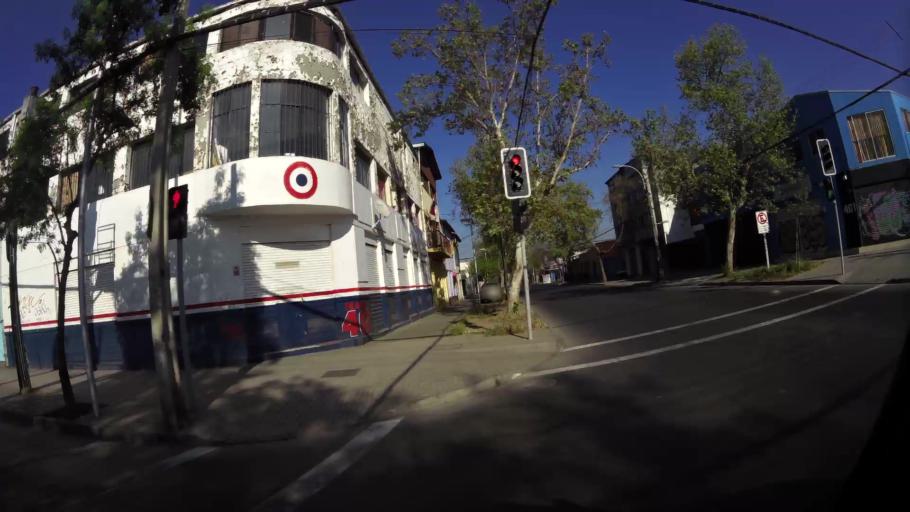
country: CL
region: Santiago Metropolitan
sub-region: Provincia de Santiago
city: Santiago
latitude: -33.4722
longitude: -70.6330
